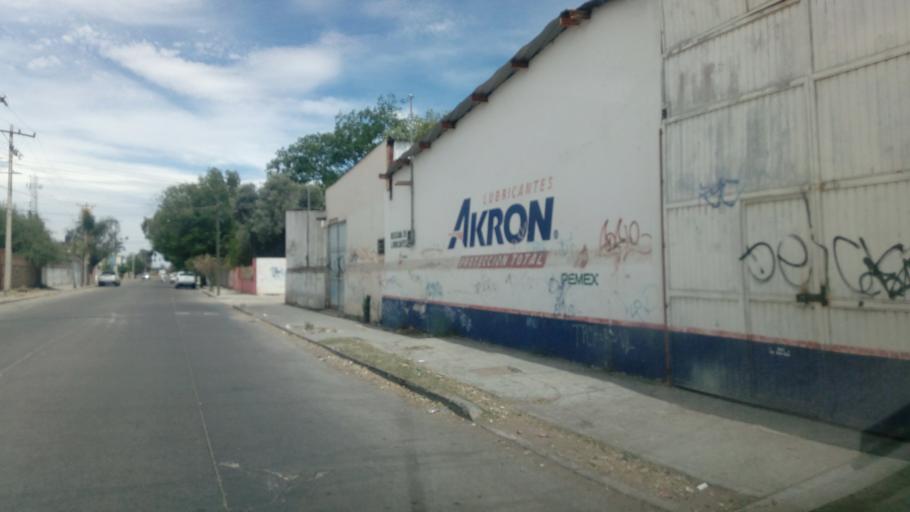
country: MX
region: Durango
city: Victoria de Durango
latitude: 23.9958
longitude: -104.6620
